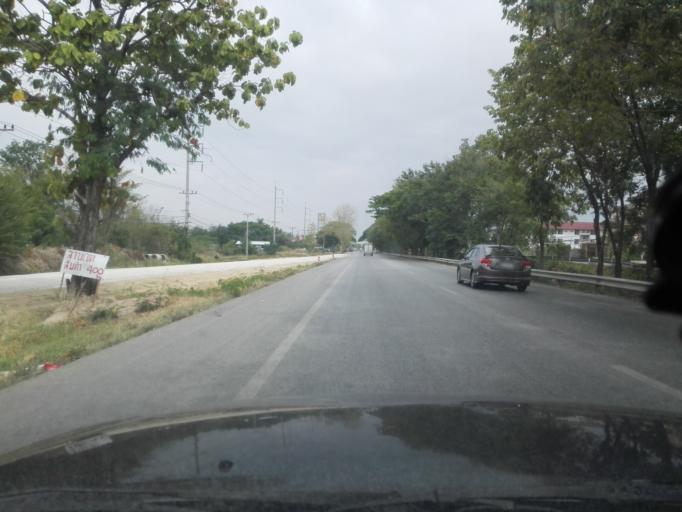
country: TH
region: Nakhon Sawan
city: Nakhon Sawan
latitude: 15.7242
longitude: 100.0462
